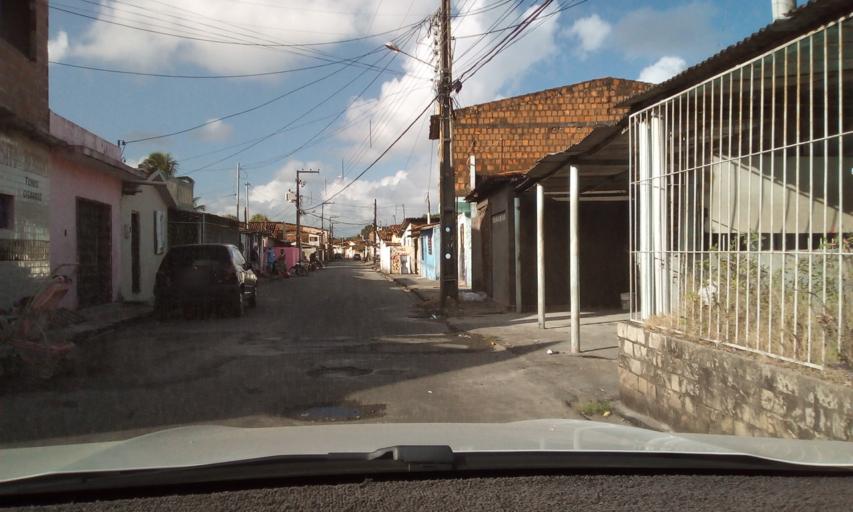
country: BR
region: Paraiba
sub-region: Joao Pessoa
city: Joao Pessoa
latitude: -7.0947
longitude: -34.8609
